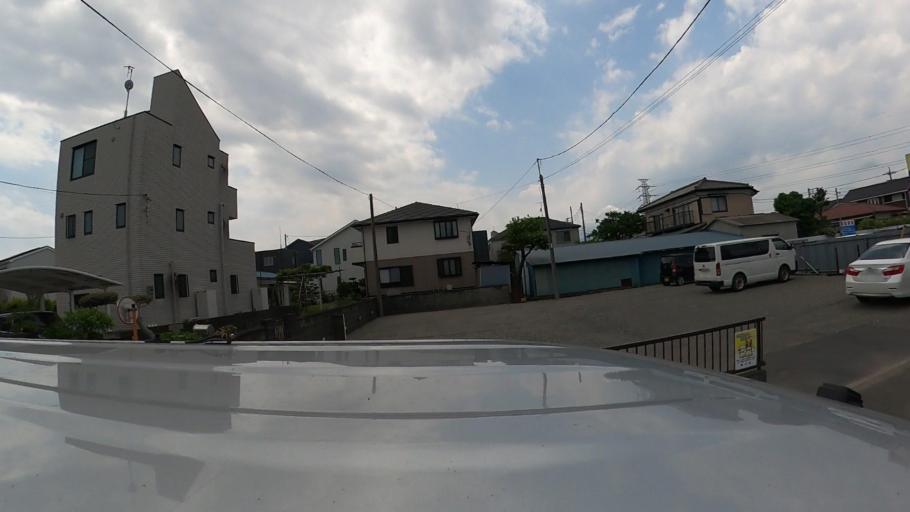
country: JP
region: Kanagawa
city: Chigasaki
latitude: 35.3649
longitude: 139.3884
